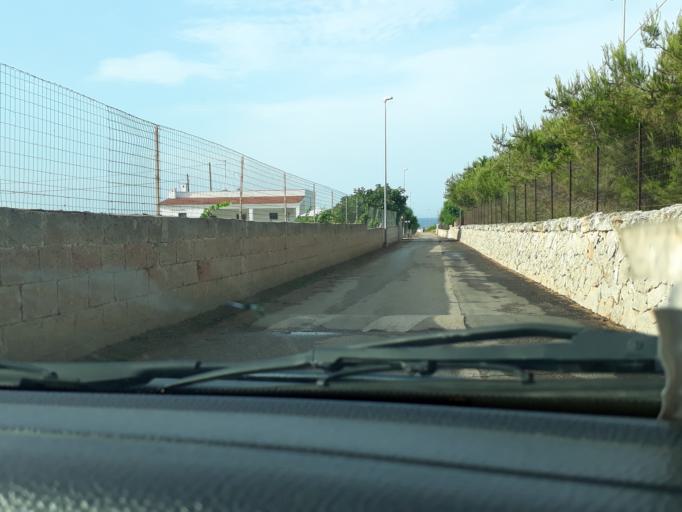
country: IT
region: Apulia
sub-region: Provincia di Brindisi
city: Carovigno
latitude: 40.7618
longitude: 17.6849
